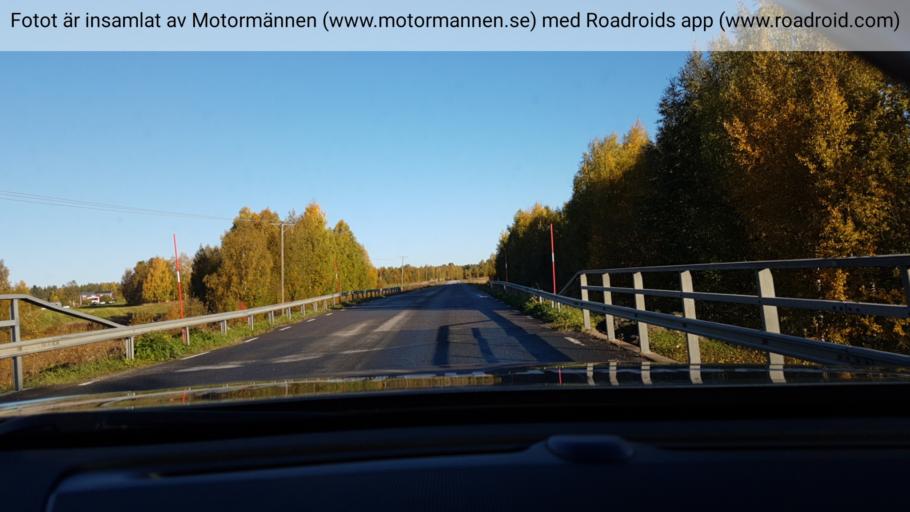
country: SE
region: Norrbotten
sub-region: Bodens Kommun
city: Boden
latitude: 65.8785
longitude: 21.6789
